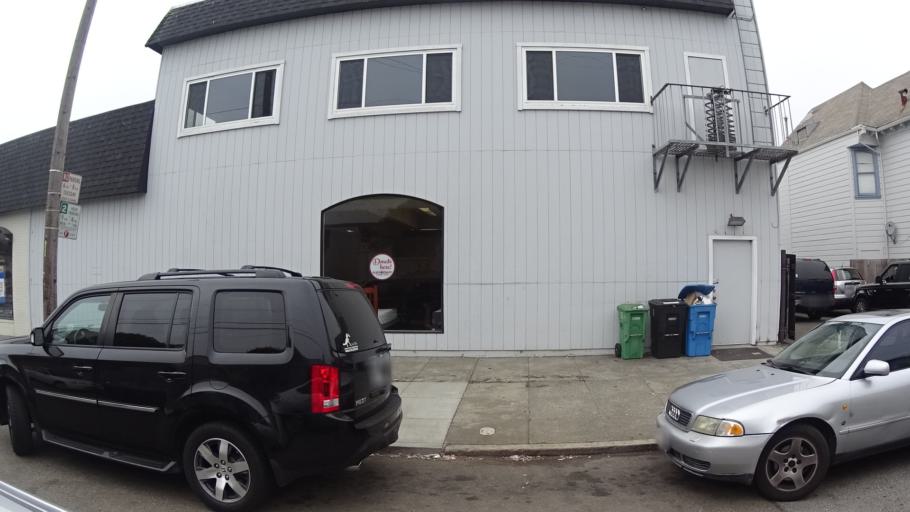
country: US
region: California
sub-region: San Francisco County
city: San Francisco
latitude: 37.7823
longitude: -122.4522
